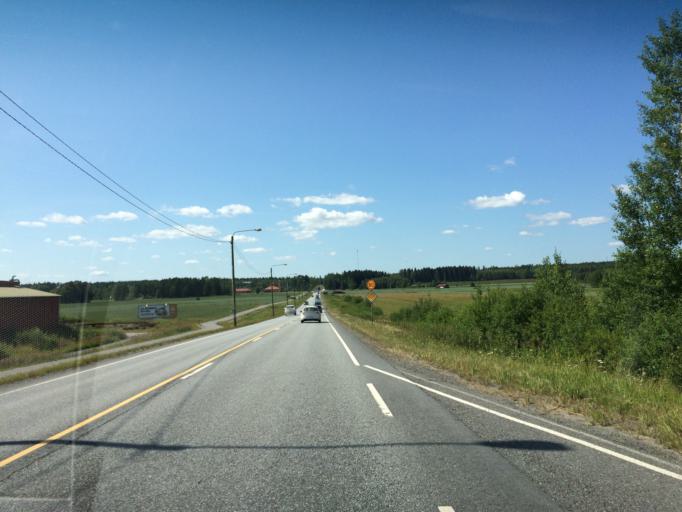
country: FI
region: Pirkanmaa
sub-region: Lounais-Pirkanmaa
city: Kiikoinen
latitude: 61.4765
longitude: 22.5736
